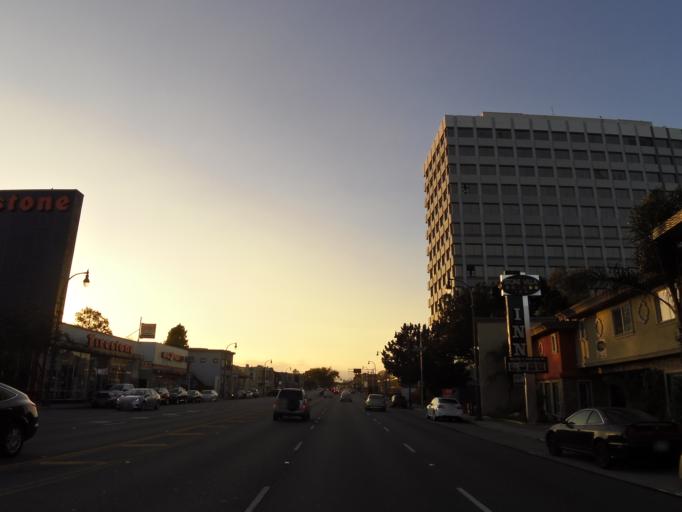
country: US
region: California
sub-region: San Mateo County
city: San Mateo
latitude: 37.5464
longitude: -122.3078
